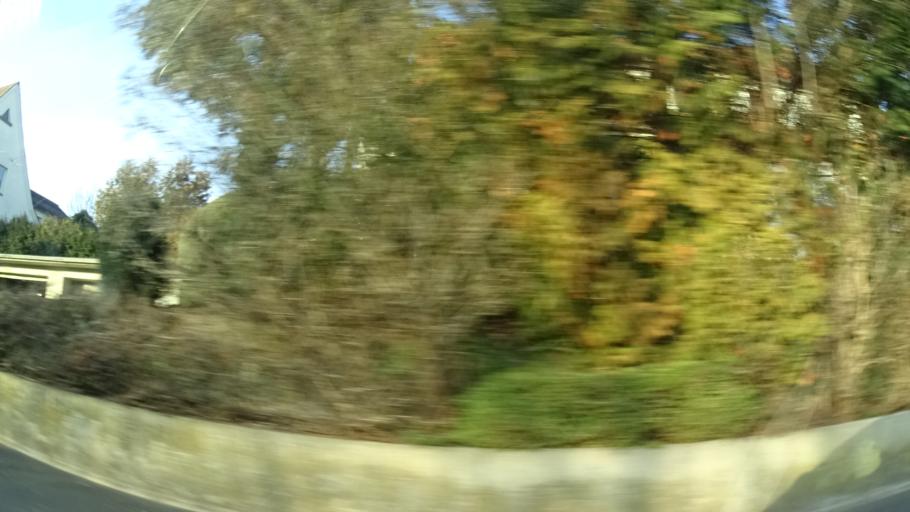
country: DE
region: Hesse
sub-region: Regierungsbezirk Darmstadt
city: Schluchtern
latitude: 50.3490
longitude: 9.5442
